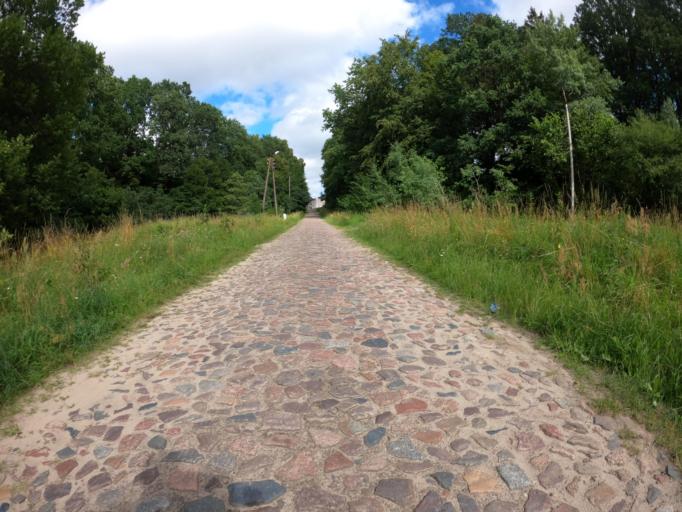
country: PL
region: West Pomeranian Voivodeship
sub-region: Powiat bialogardzki
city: Tychowo
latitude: 54.0216
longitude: 16.3543
